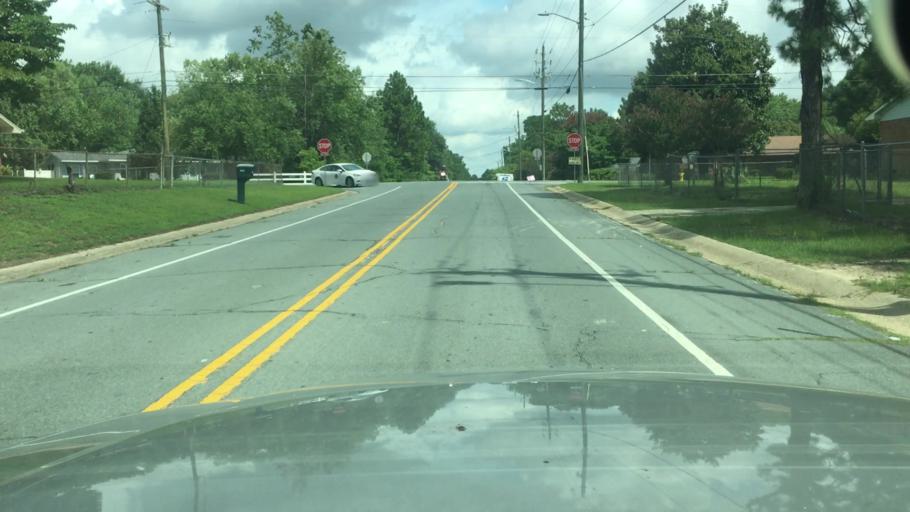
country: US
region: North Carolina
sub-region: Cumberland County
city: Hope Mills
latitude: 35.0209
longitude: -78.9357
